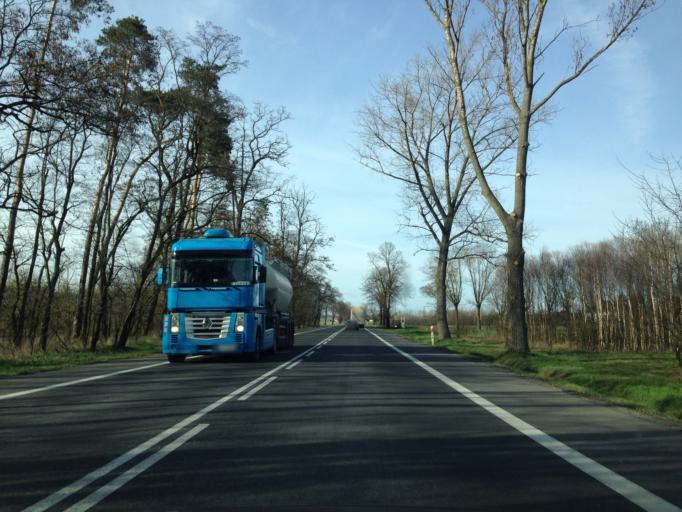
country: PL
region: Kujawsko-Pomorskie
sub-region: Powiat wloclawski
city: Lubien Kujawski
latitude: 52.3871
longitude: 19.1688
